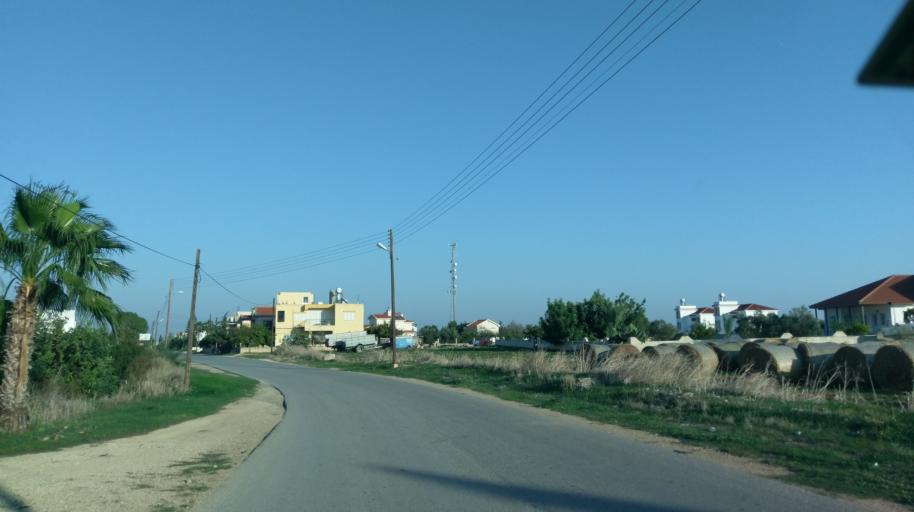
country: CY
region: Ammochostos
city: Leonarisso
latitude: 35.4215
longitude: 34.0785
